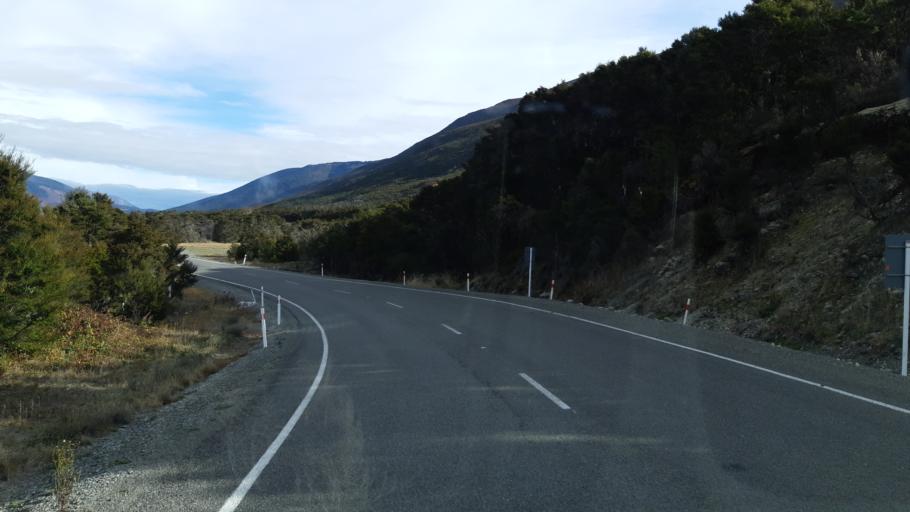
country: NZ
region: Tasman
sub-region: Tasman District
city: Wakefield
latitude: -41.7295
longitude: 173.0370
